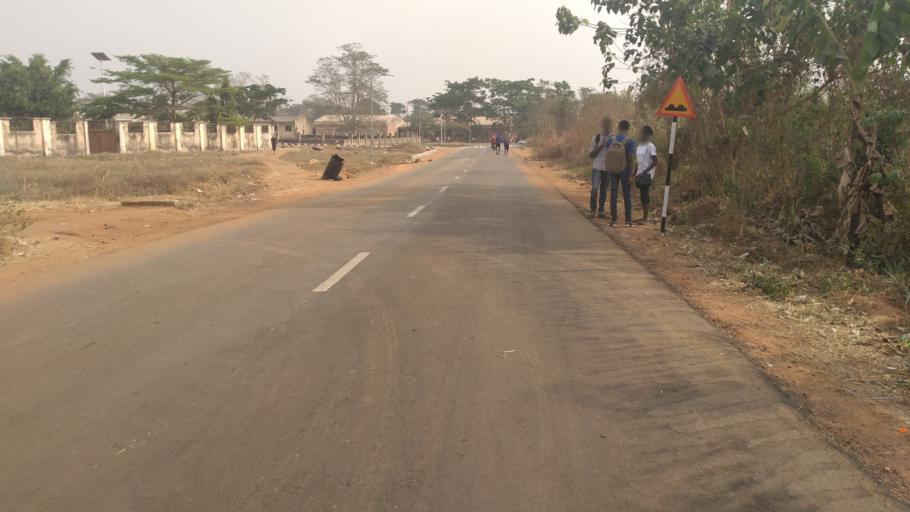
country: NG
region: Ondo
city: Ilare
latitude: 7.2980
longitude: 5.1455
